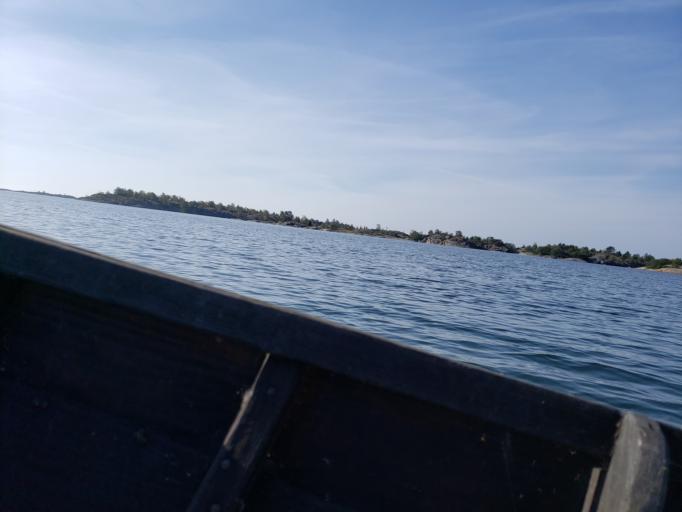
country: FI
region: Varsinais-Suomi
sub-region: Aboland-Turunmaa
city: Dragsfjaerd
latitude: 59.8564
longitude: 22.2109
